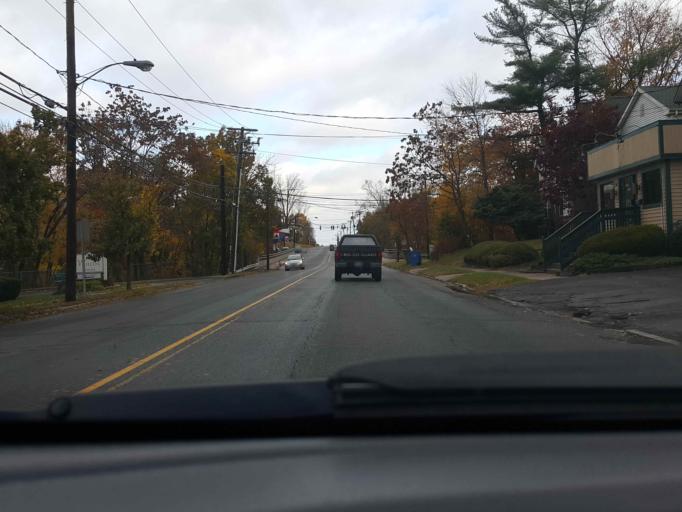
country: US
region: Connecticut
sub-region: Middlesex County
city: Middletown
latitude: 41.5482
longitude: -72.6506
